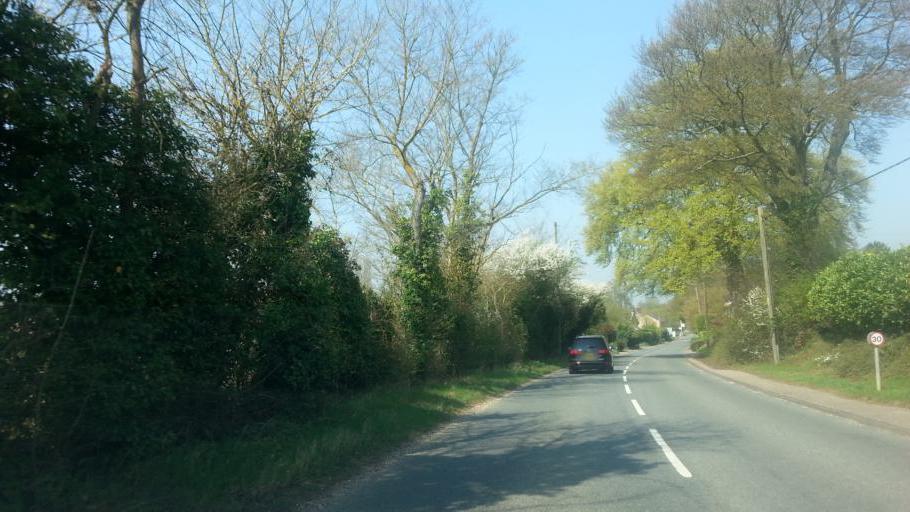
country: GB
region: England
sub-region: Suffolk
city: Thurston
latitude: 52.2321
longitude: 0.8394
